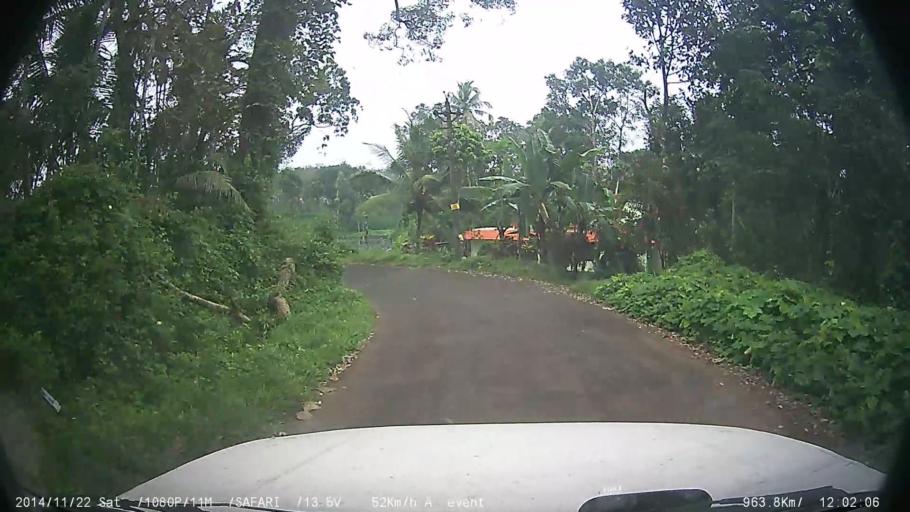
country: IN
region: Kerala
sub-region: Kottayam
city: Palackattumala
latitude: 9.7832
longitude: 76.5645
